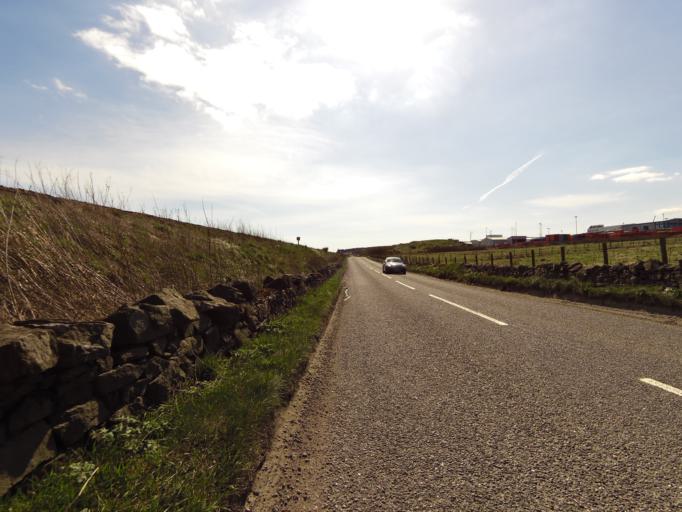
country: GB
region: Scotland
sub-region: Aberdeen City
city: Aberdeen
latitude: 57.1193
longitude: -2.0601
